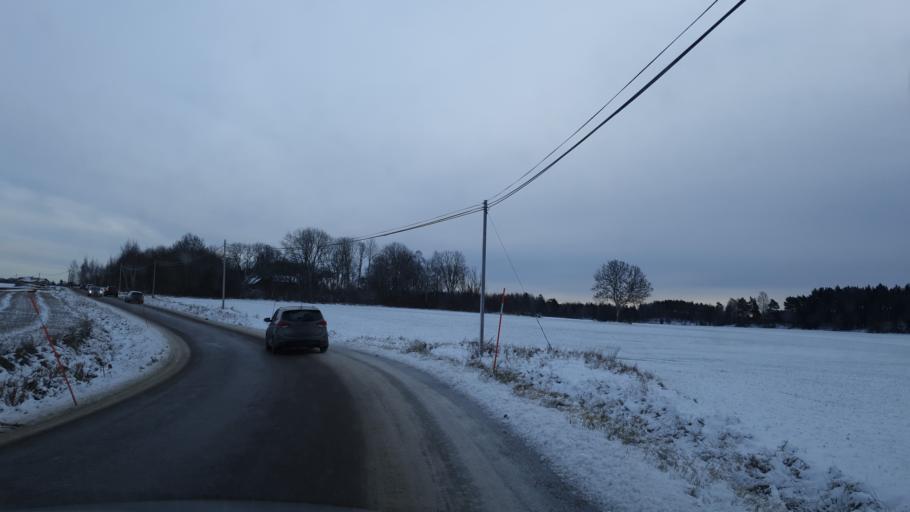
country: SE
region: Uppsala
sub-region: Habo Kommun
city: Balsta
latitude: 59.7081
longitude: 17.5694
